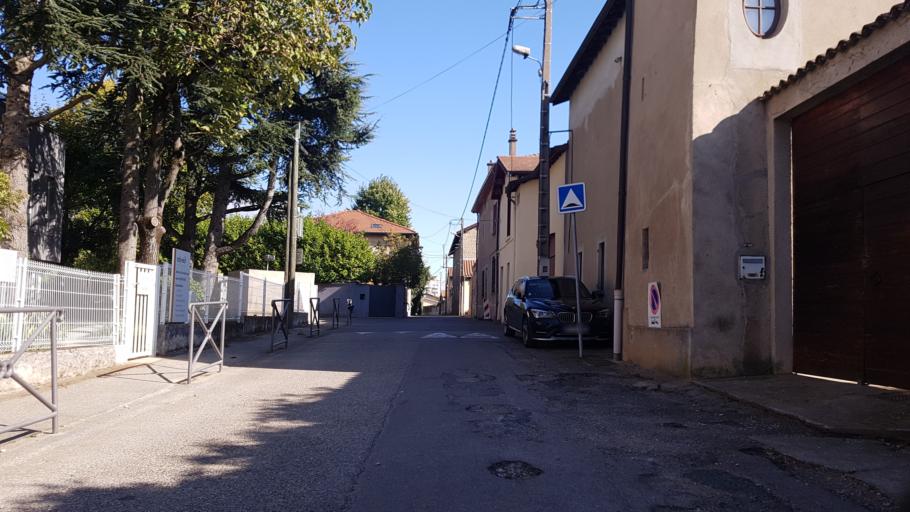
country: FR
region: Rhone-Alpes
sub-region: Departement du Rhone
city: Ecully
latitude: 45.7858
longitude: 4.7870
